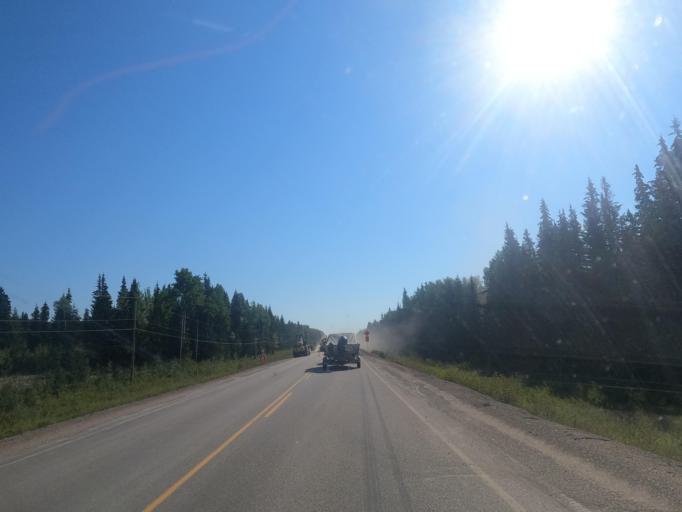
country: CA
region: British Columbia
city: Burns Lake
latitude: 54.1018
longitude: -125.3302
